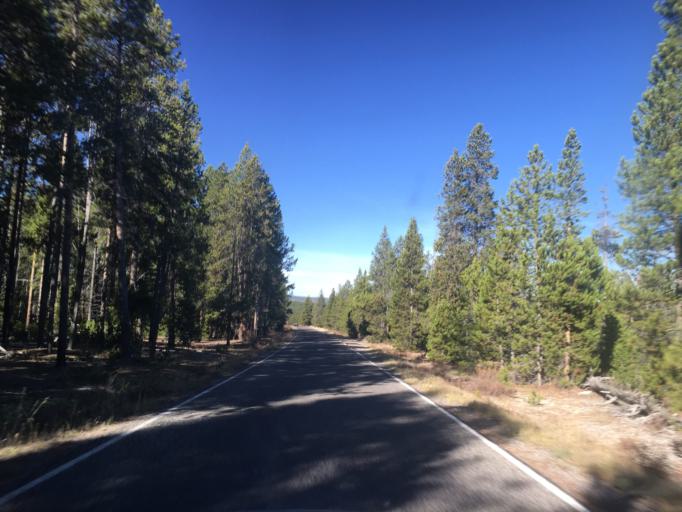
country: US
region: Montana
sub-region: Gallatin County
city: West Yellowstone
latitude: 44.5471
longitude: -110.7974
